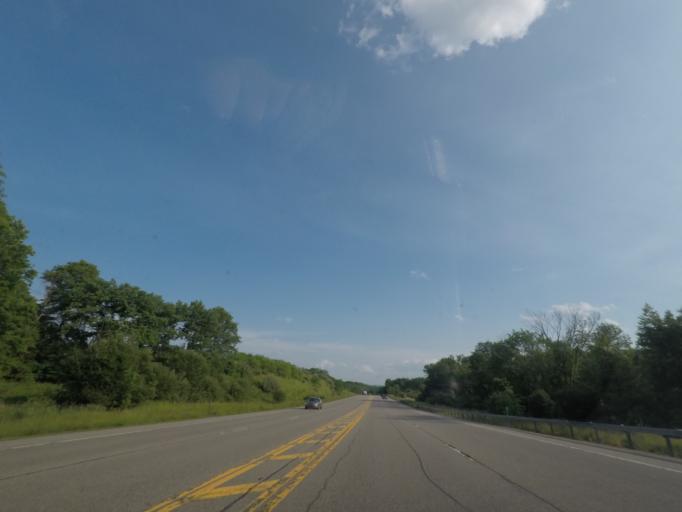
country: US
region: New York
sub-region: Orange County
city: Orange Lake
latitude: 41.5030
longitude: -74.1351
